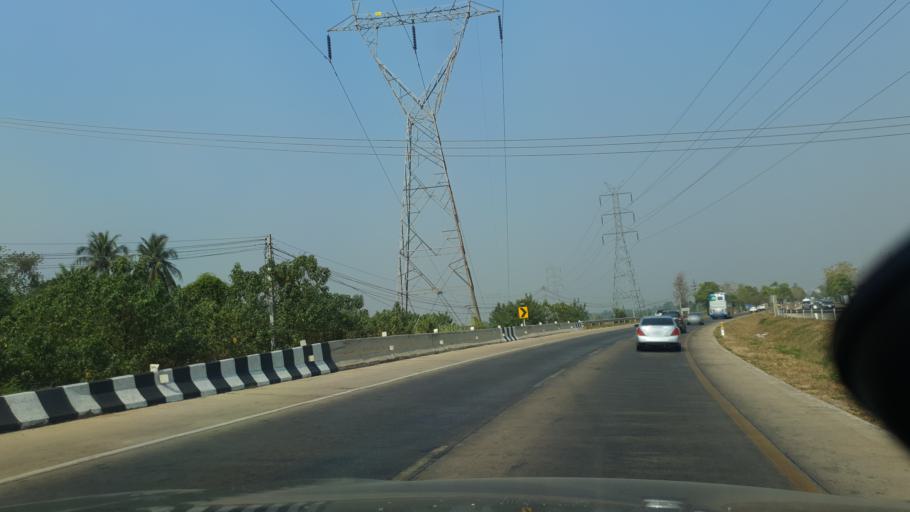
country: TH
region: Kamphaeng Phet
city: Kamphaeng Phet
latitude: 16.4564
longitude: 99.4952
